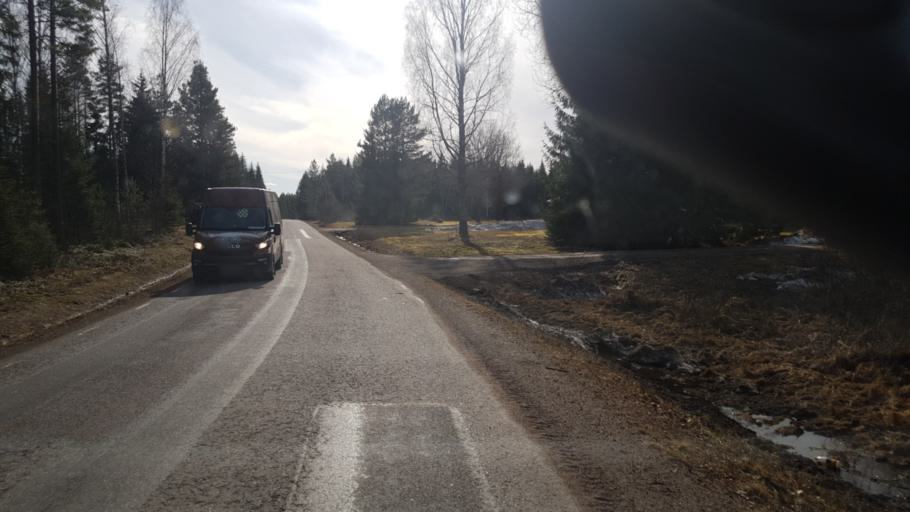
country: SE
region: Vaermland
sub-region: Eda Kommun
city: Charlottenberg
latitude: 59.8526
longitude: 12.3203
